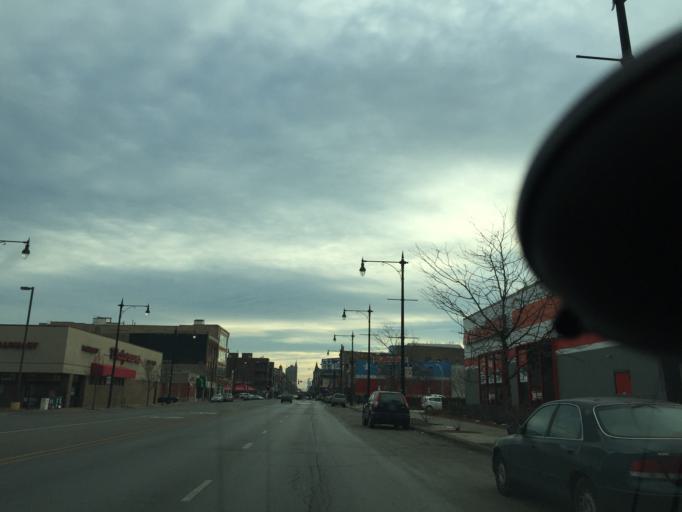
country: US
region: Illinois
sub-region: Cook County
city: Chicago
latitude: 41.9102
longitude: -87.6898
